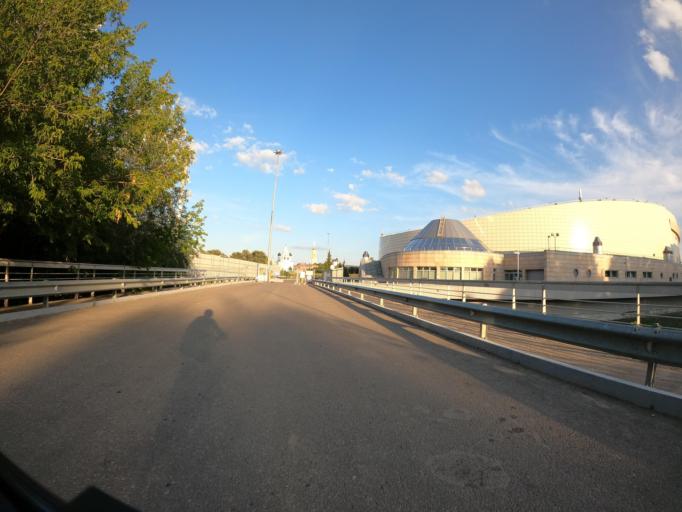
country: RU
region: Moskovskaya
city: Raduzhnyy
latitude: 55.1079
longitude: 38.7514
